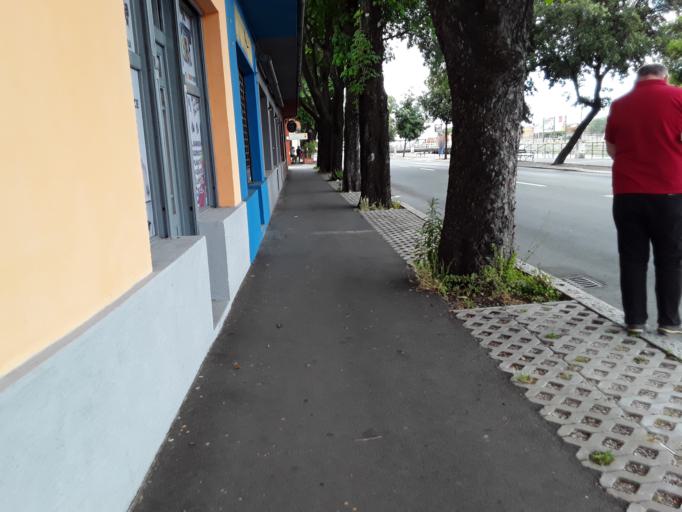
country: HR
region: Primorsko-Goranska
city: Drenova
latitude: 45.3249
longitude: 14.4489
